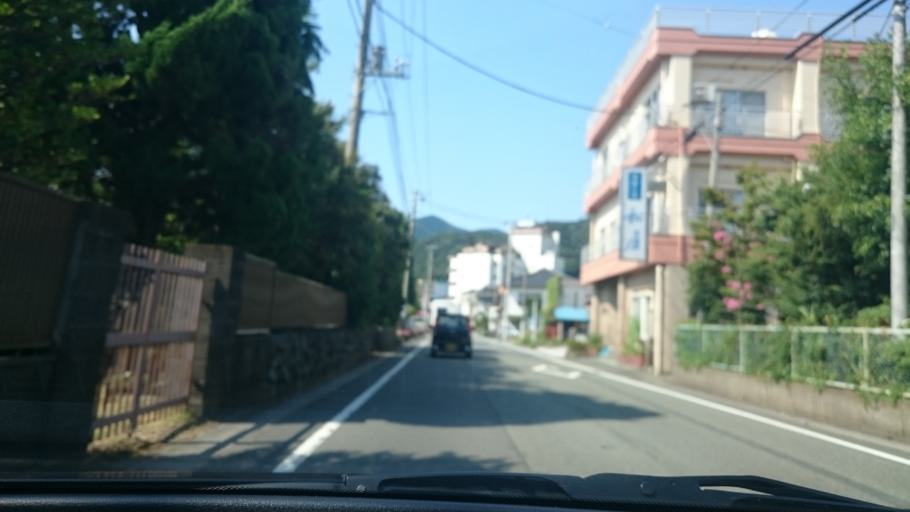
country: JP
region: Shizuoka
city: Heda
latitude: 34.9091
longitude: 138.7916
